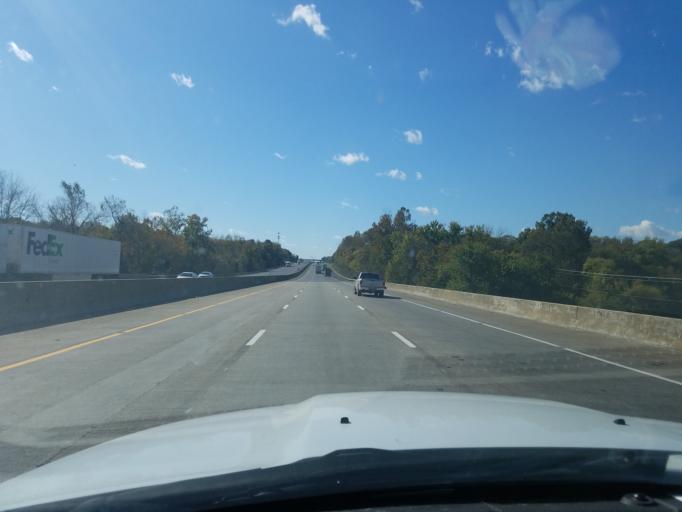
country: US
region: Kentucky
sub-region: Warren County
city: Bowling Green
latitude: 36.9887
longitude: -86.3851
